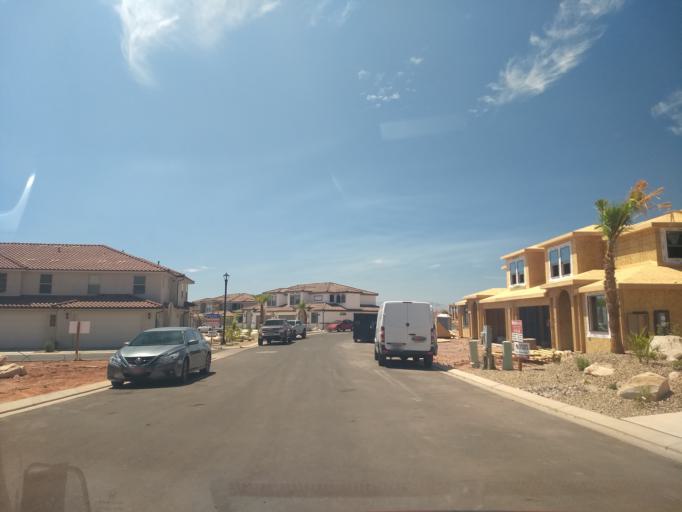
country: US
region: Utah
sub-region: Washington County
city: Washington
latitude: 37.1472
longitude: -113.4719
